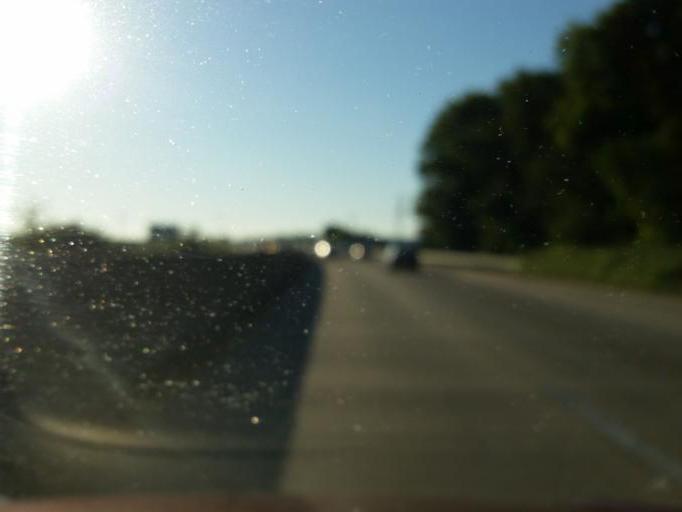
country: US
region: Pennsylvania
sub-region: Lancaster County
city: East Petersburg
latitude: 40.0854
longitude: -76.3732
